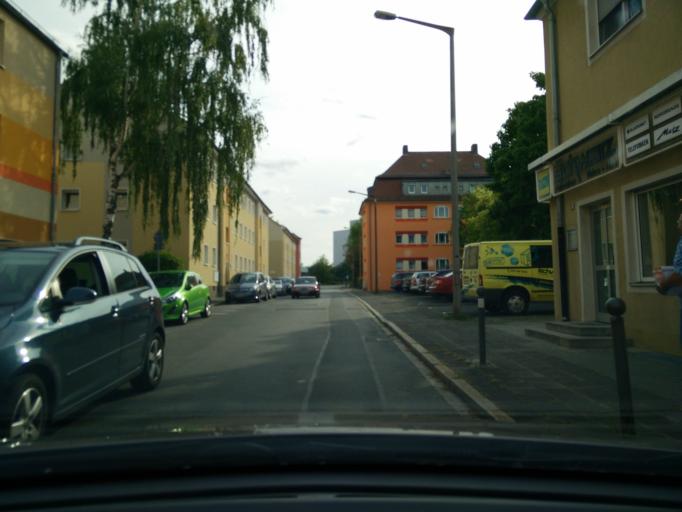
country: DE
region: Bavaria
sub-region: Regierungsbezirk Mittelfranken
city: Grossreuth bei Schweinau
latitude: 49.4278
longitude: 11.0514
